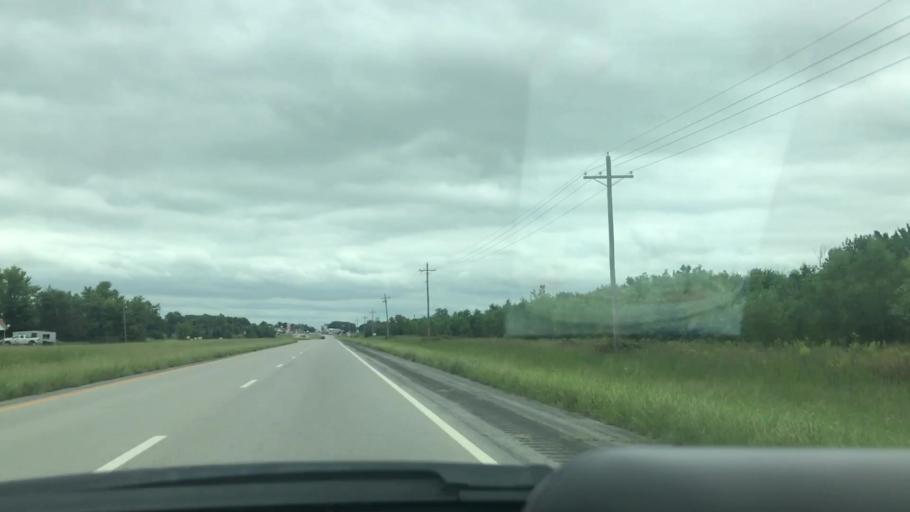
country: US
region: Oklahoma
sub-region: Mayes County
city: Pryor
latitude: 36.4253
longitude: -95.2758
